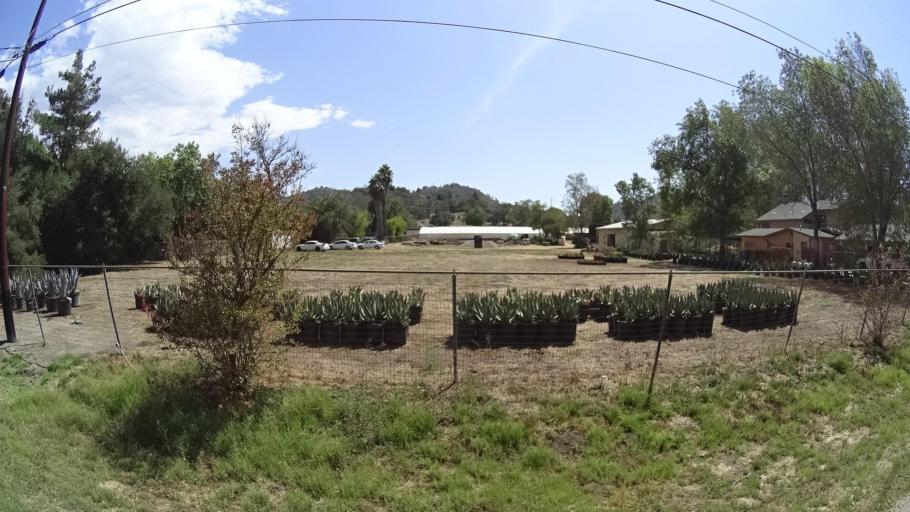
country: US
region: California
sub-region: San Diego County
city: Valley Center
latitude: 33.2100
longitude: -117.0290
